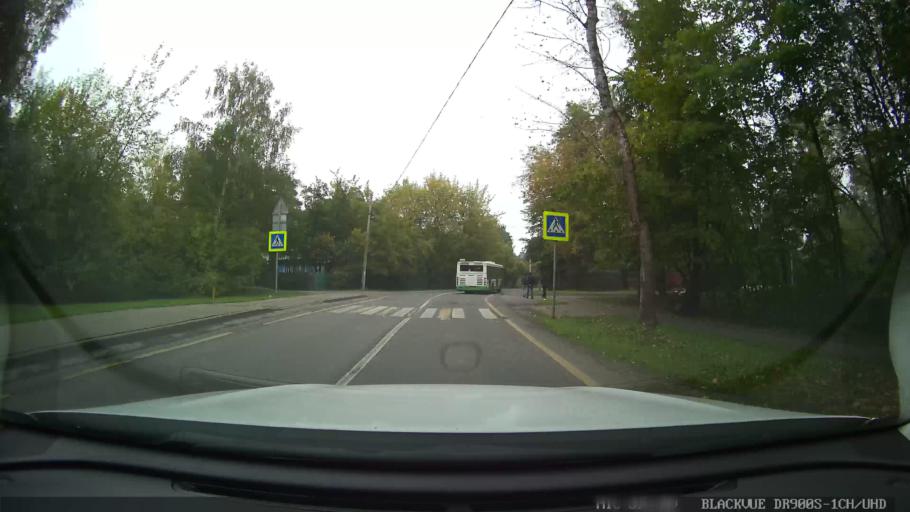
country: RU
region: Moscow
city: Novo-Peredelkino
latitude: 55.6546
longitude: 37.3542
